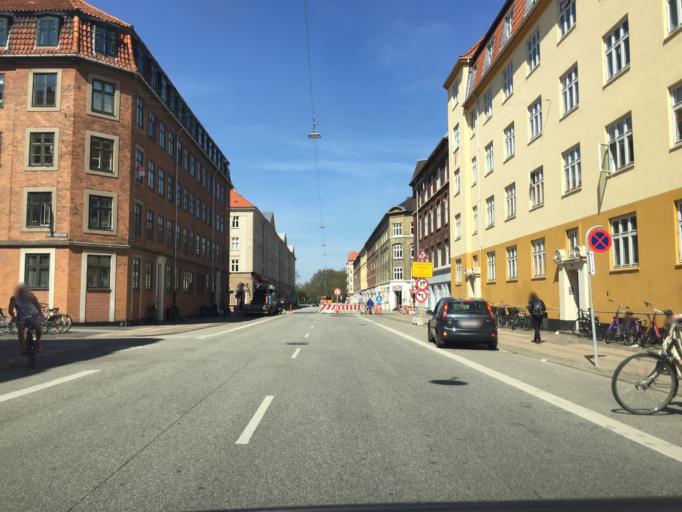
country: DK
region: Capital Region
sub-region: Kobenhavn
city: Copenhagen
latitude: 55.7121
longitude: 12.5692
